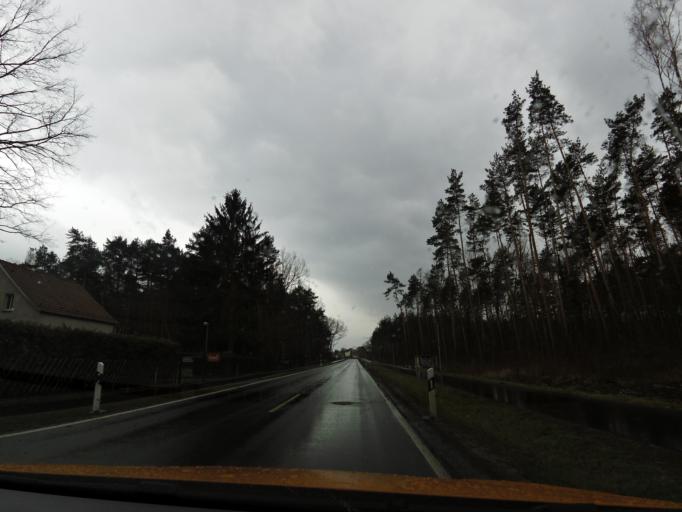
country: DE
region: Berlin
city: Lichtenrade
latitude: 52.3434
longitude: 13.4008
